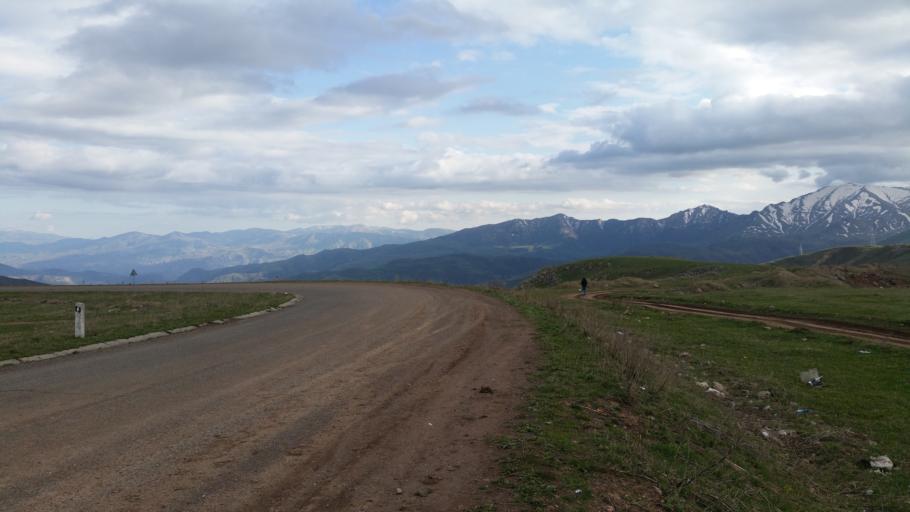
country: AM
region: Geghark'unik'i Marz
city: Madina
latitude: 39.9525
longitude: 45.2338
